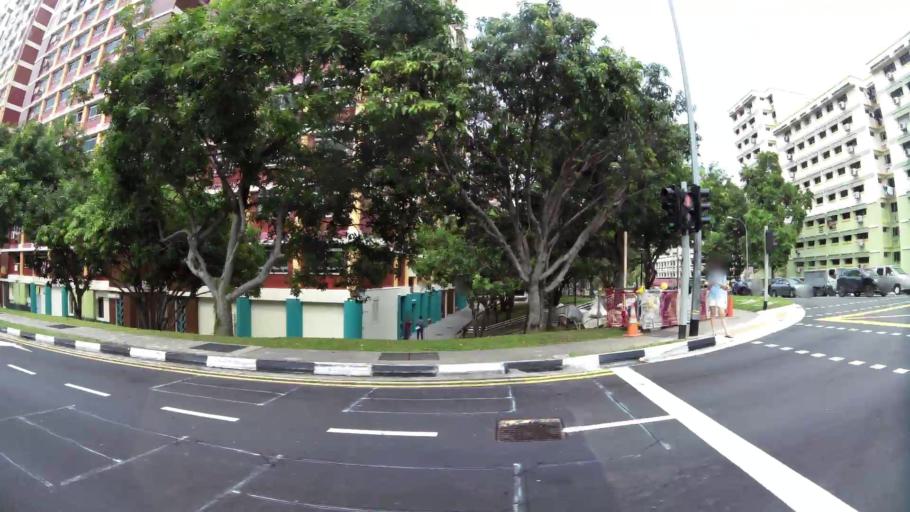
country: SG
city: Singapore
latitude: 1.3313
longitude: 103.9070
